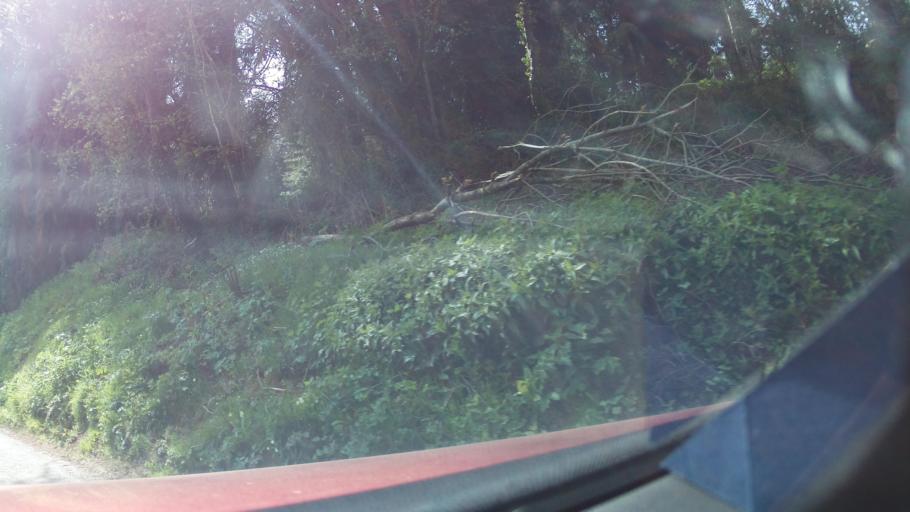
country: GB
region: England
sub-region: Dorset
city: Sherborne
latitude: 50.9722
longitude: -2.5328
